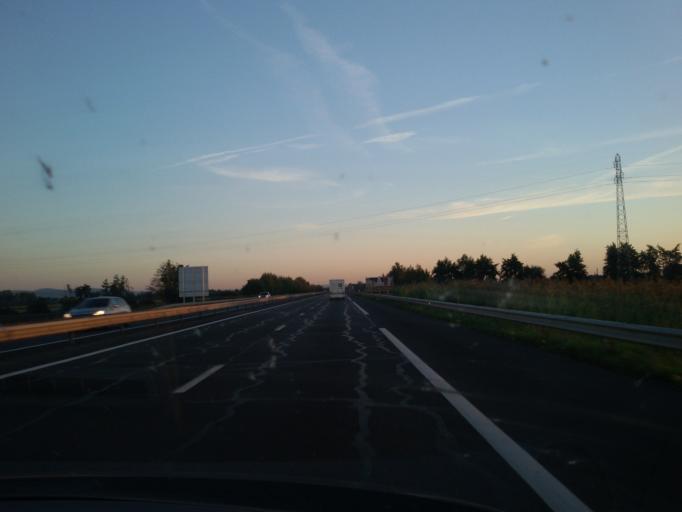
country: FR
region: Auvergne
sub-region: Departement du Puy-de-Dome
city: Menetrol
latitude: 45.8620
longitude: 3.1584
